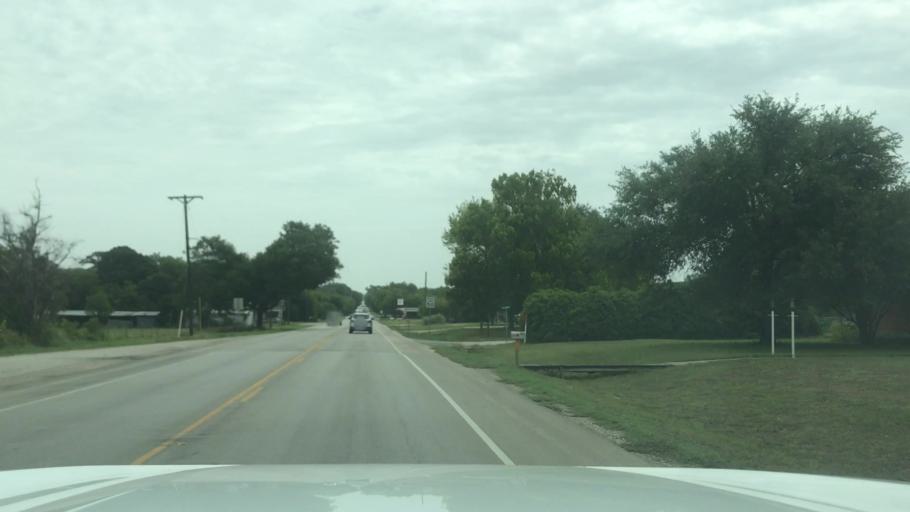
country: US
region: Texas
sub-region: Erath County
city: Dublin
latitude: 32.0880
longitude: -98.3547
